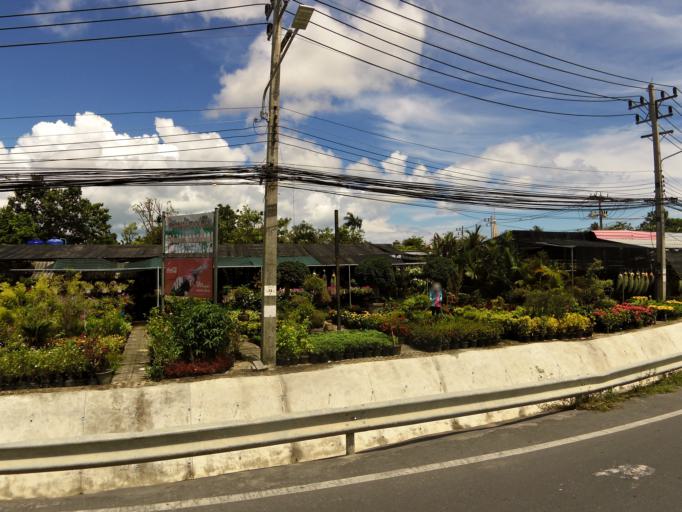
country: TH
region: Phuket
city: Ban Chalong
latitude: 7.8492
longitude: 98.3340
